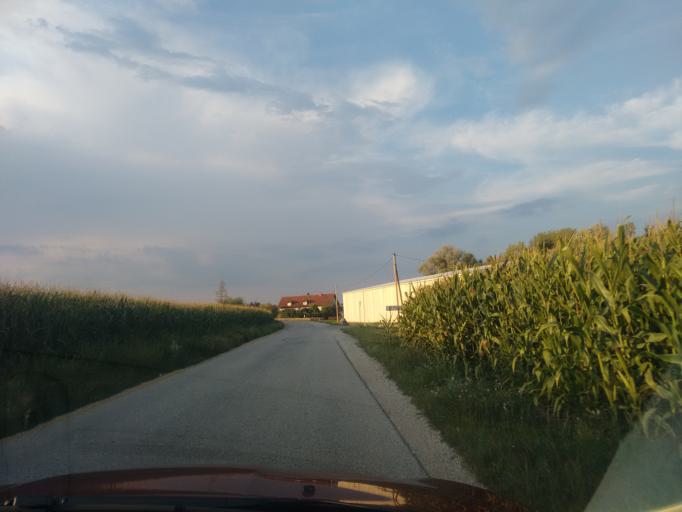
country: AT
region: Upper Austria
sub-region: Politischer Bezirk Grieskirchen
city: Bad Schallerbach
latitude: 48.1989
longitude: 13.9206
